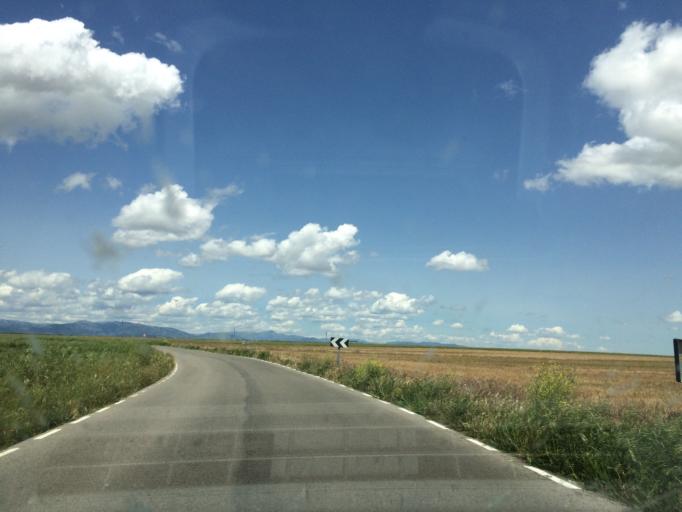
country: ES
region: Madrid
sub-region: Provincia de Madrid
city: Ribatejada
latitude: 40.7121
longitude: -3.4230
